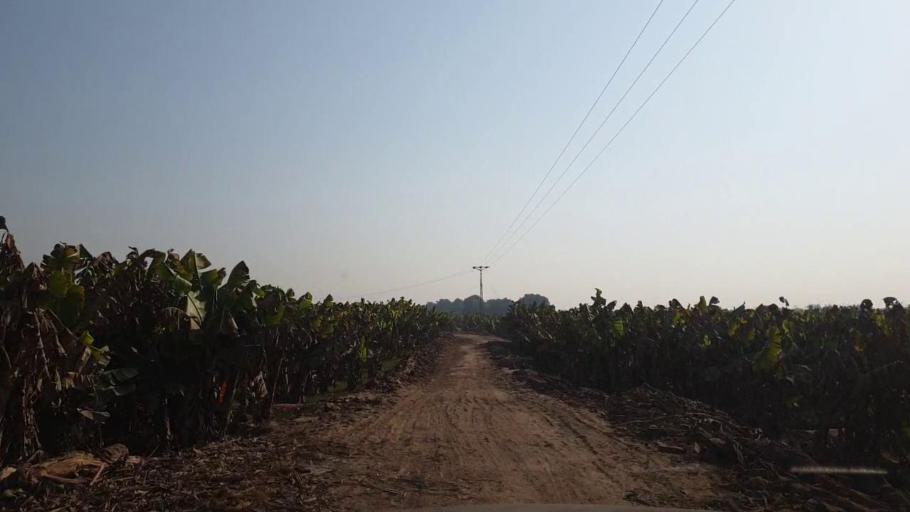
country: PK
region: Sindh
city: Tando Allahyar
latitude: 25.5095
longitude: 68.7310
